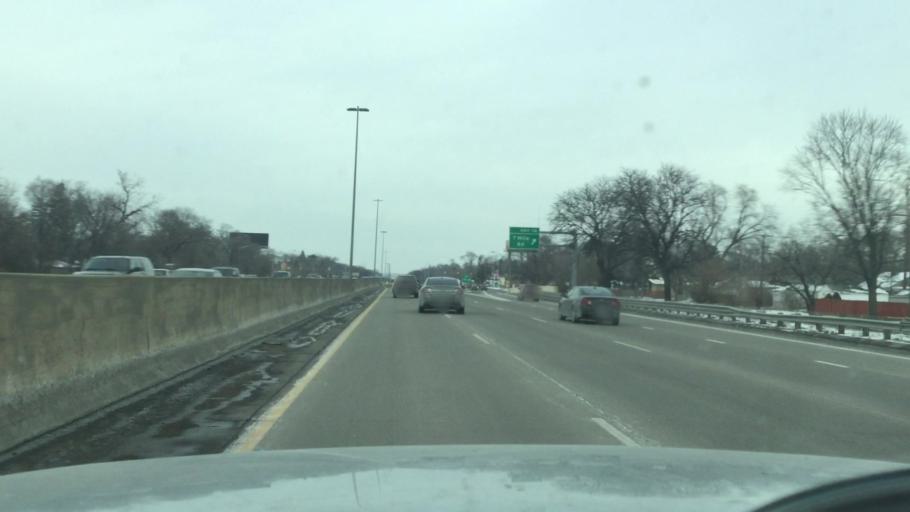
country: US
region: Michigan
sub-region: Oakland County
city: Southfield
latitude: 42.4262
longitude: -83.2191
